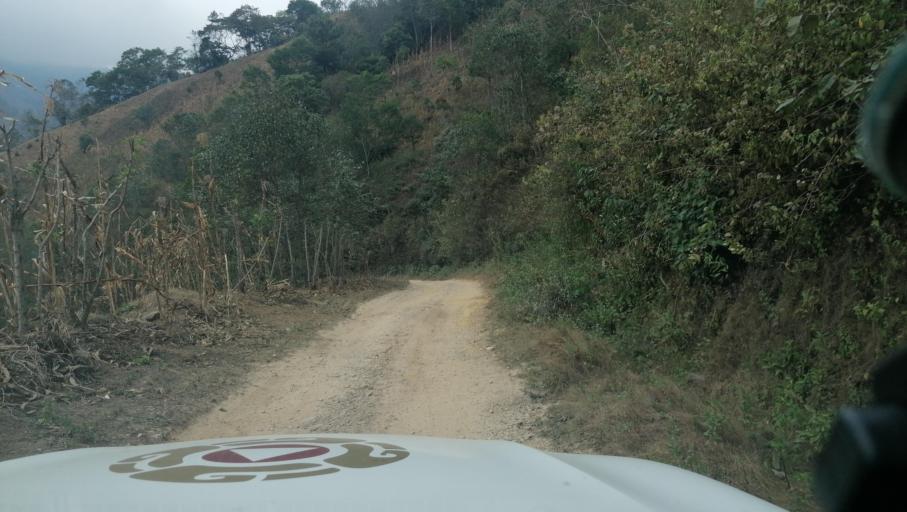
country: GT
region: San Marcos
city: Tacana
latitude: 15.2176
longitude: -92.1992
